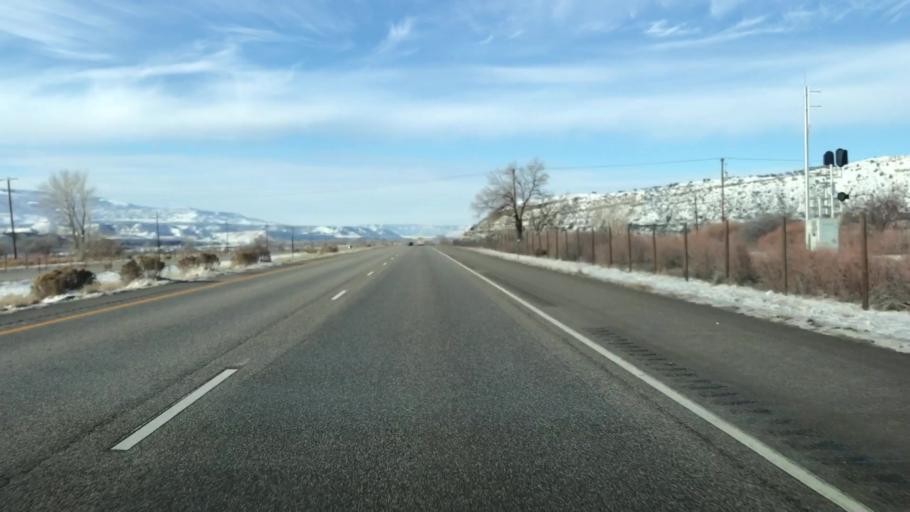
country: US
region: Colorado
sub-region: Garfield County
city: Silt
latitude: 39.5488
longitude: -107.6100
